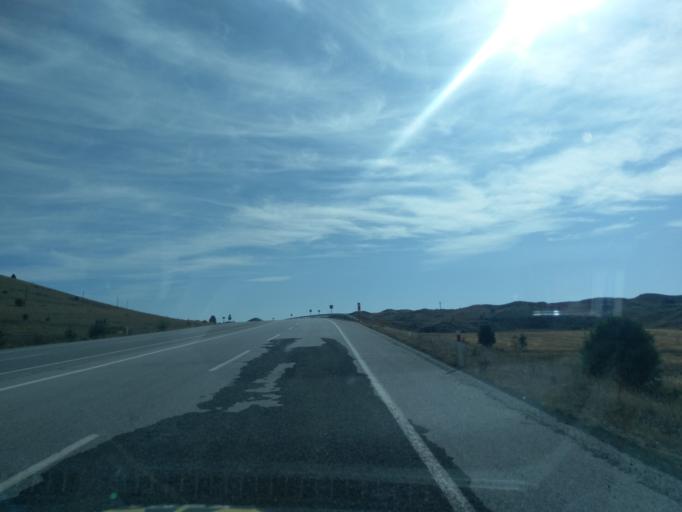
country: TR
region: Sivas
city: Imranli
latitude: 39.8834
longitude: 38.0443
